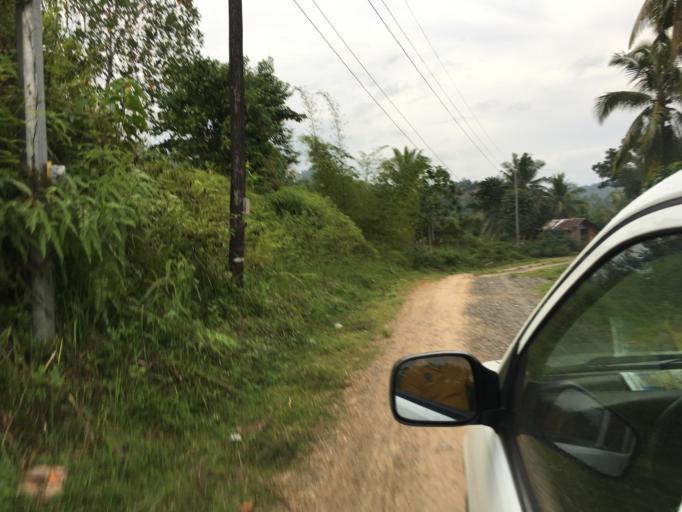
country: PH
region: Western Visayas
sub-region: Province of Aklan
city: Lupo
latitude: 11.4842
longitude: 122.5048
